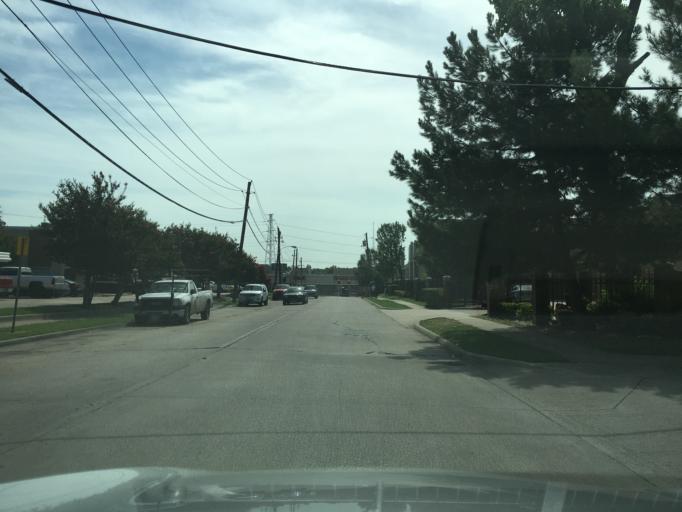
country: US
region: Texas
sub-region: Dallas County
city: Richardson
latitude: 32.9307
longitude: -96.7629
